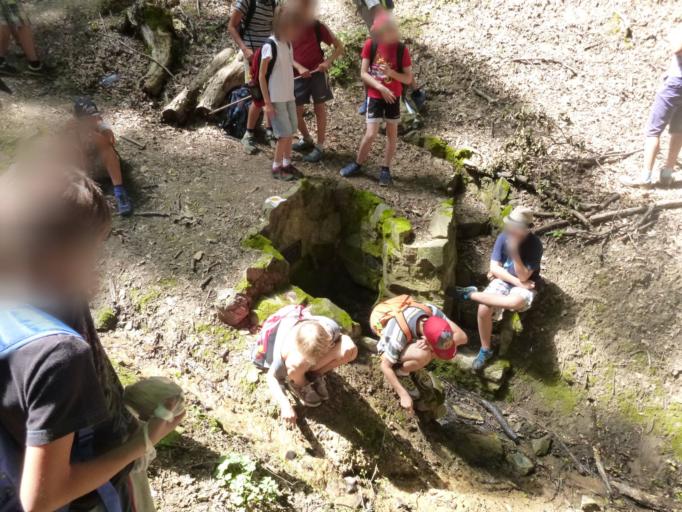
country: HU
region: Baranya
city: Szaszvar
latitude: 46.2410
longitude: 18.3544
